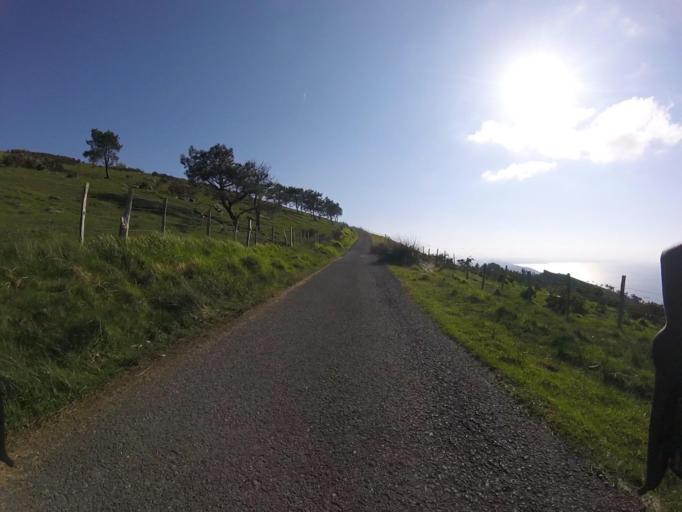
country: ES
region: Basque Country
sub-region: Provincia de Guipuzcoa
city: Lezo
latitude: 43.3494
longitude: -1.8511
